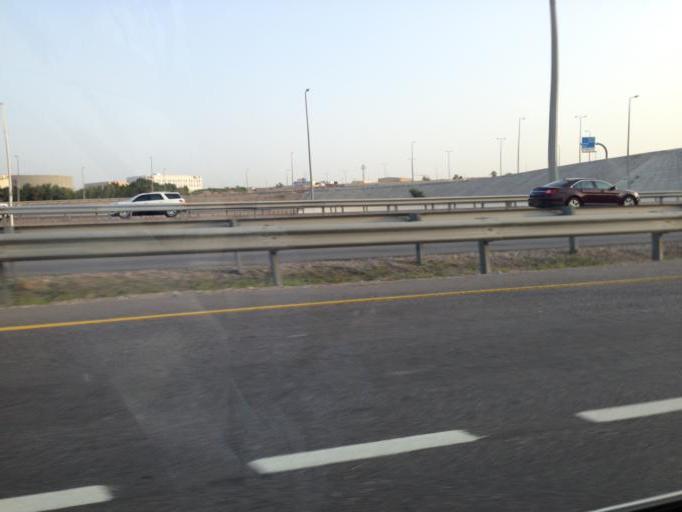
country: OM
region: Muhafazat Masqat
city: Bawshar
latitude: 23.5605
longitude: 58.3379
